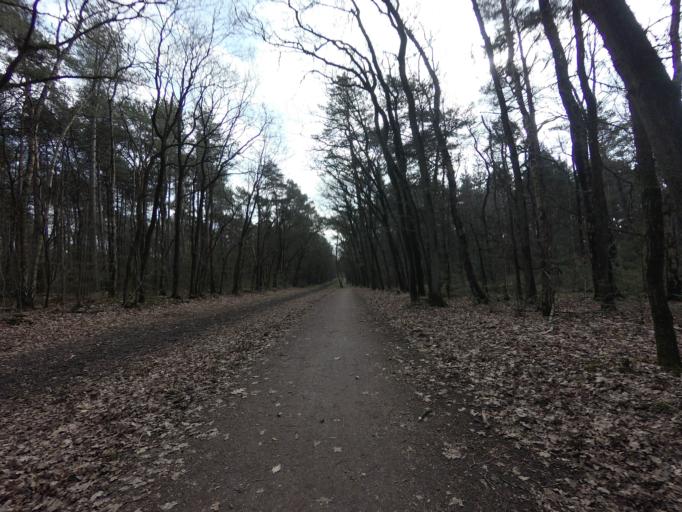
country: NL
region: North Holland
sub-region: Gemeente Bussum
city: Bussum
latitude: 52.2465
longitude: 5.1495
